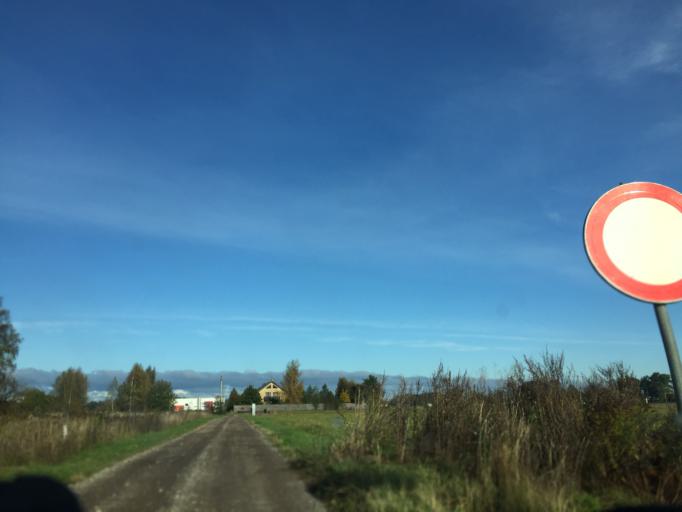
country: LV
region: Adazi
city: Adazi
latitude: 57.0919
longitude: 24.3082
